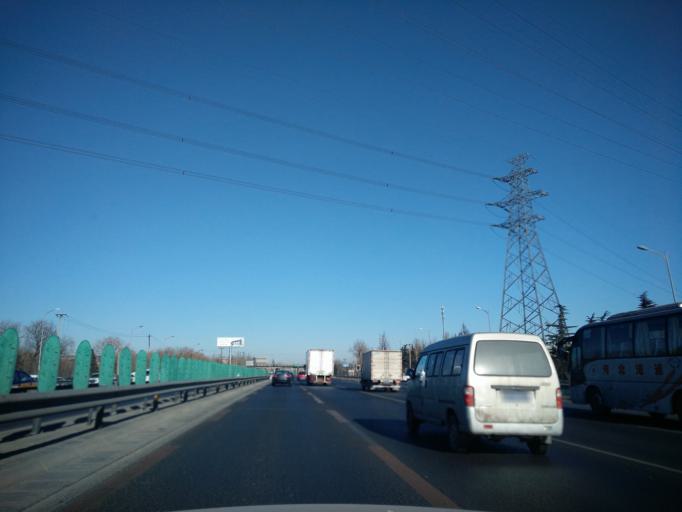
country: CN
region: Beijing
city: Xihongmen
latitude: 39.8042
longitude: 116.3395
